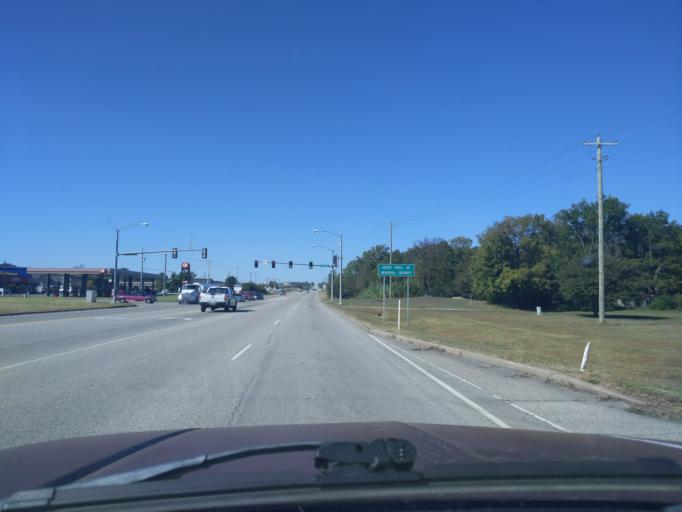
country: US
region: Oklahoma
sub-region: Tulsa County
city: Glenpool
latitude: 35.9884
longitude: -96.0154
